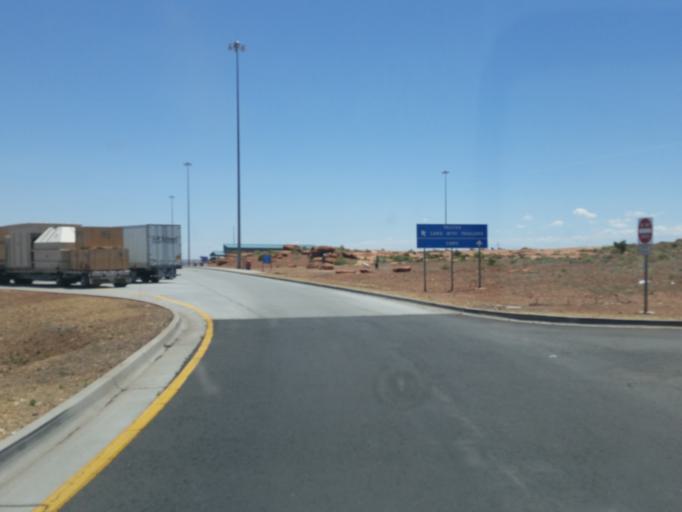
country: US
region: Arizona
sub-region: Coconino County
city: LeChee
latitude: 35.1054
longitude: -111.0067
